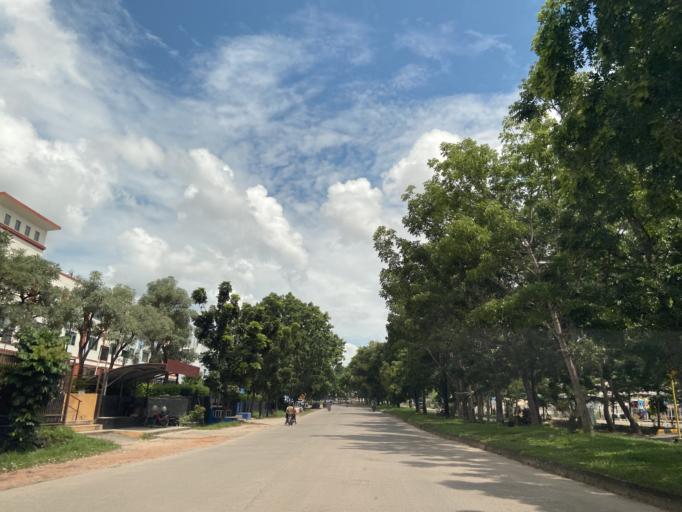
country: SG
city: Singapore
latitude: 1.1410
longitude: 104.0019
